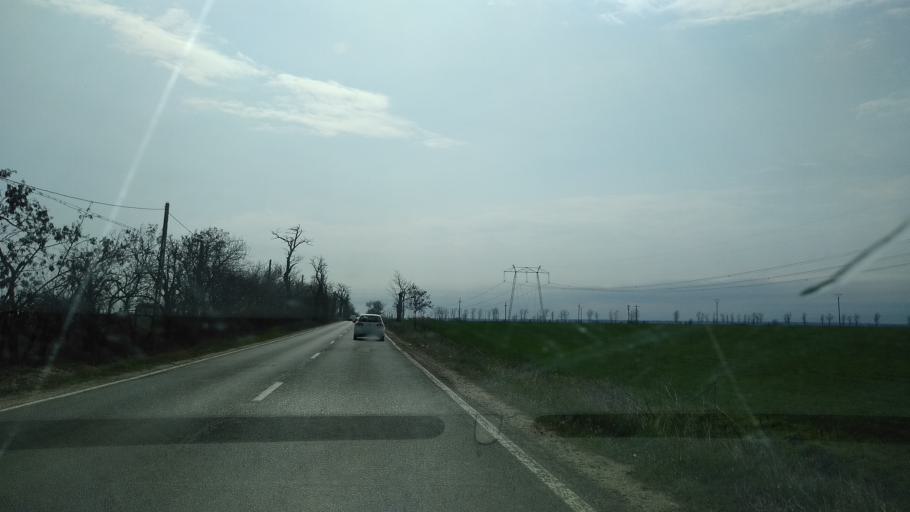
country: RO
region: Giurgiu
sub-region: Comuna Herasti
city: Herasti
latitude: 44.2565
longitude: 26.3613
